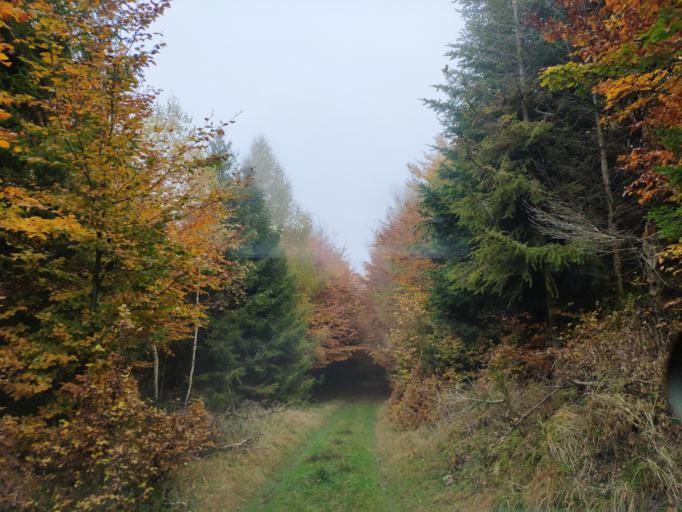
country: SK
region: Kosicky
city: Medzev
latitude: 48.7381
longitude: 20.9933
